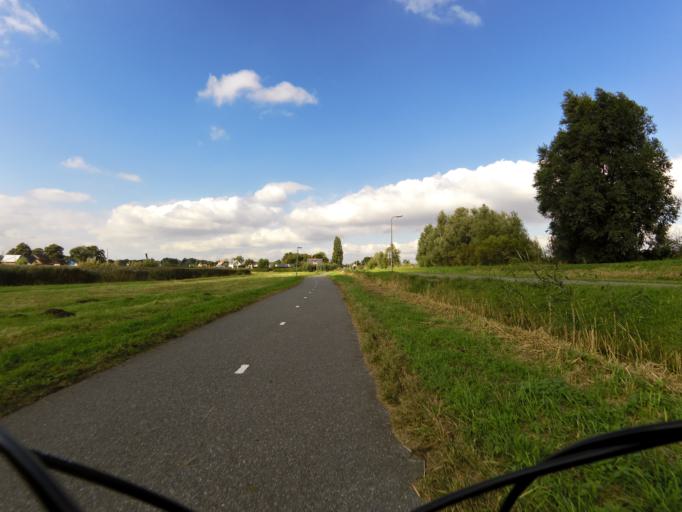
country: NL
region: South Holland
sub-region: Gemeente Voorschoten
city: Voorschoten
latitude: 52.1035
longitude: 4.4385
